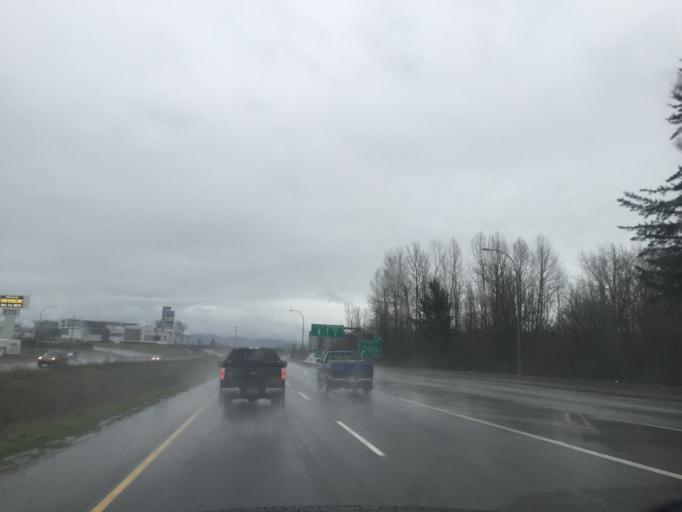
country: CA
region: British Columbia
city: Aldergrove
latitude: 49.0597
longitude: -122.3867
